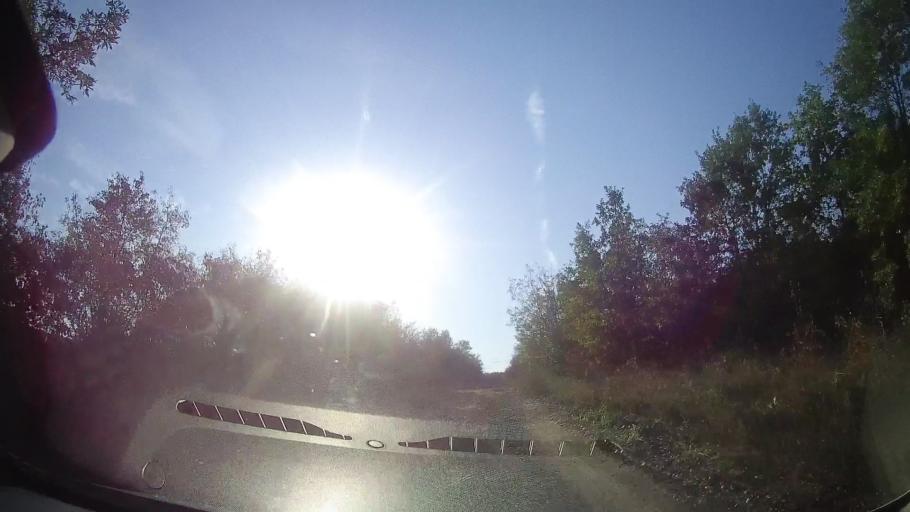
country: RO
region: Timis
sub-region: Comuna Bogda
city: Bogda
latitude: 45.9493
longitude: 21.6180
